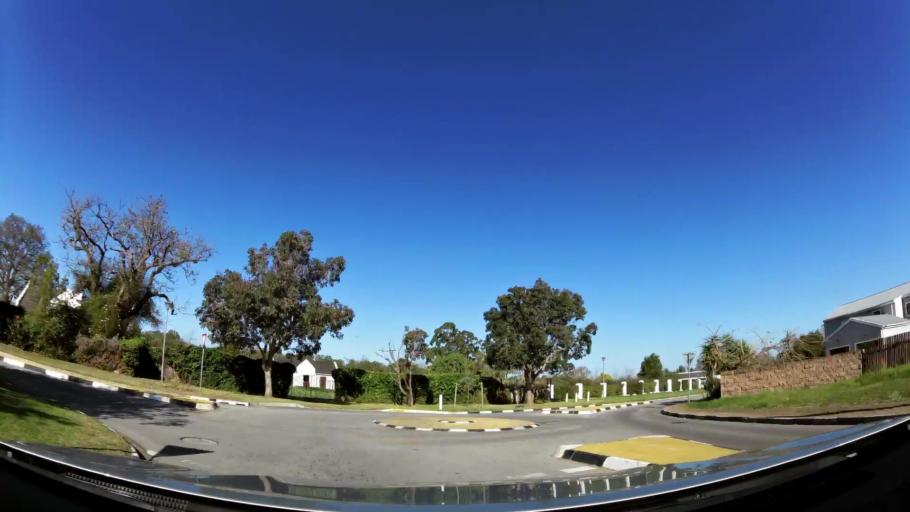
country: ZA
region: Western Cape
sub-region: Eden District Municipality
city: George
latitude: -33.9498
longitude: 22.4146
